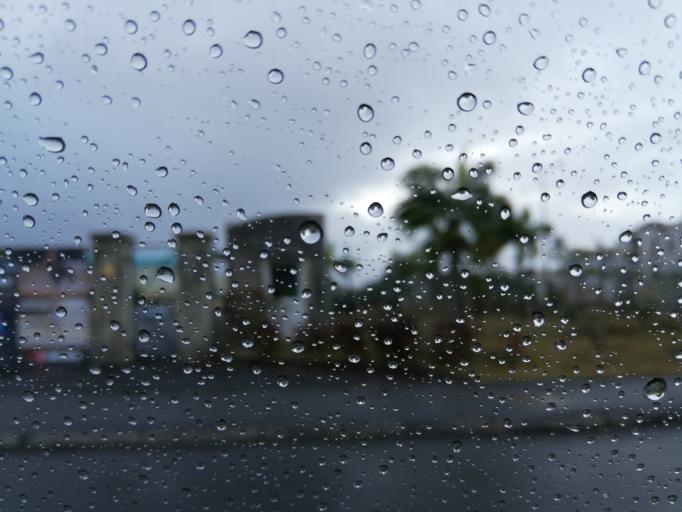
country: MU
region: Plaines Wilhems
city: Ebene
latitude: -20.2485
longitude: 57.4888
